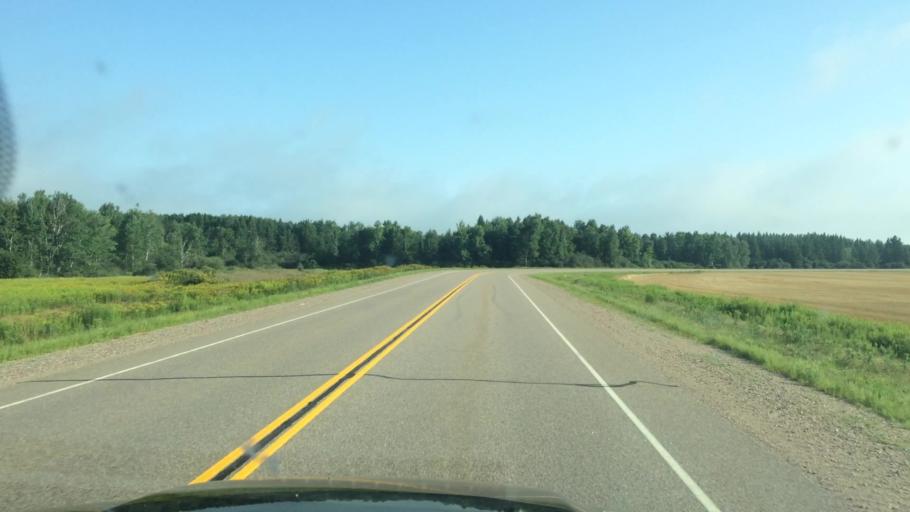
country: US
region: Wisconsin
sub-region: Langlade County
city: Antigo
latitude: 45.1478
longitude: -89.1846
